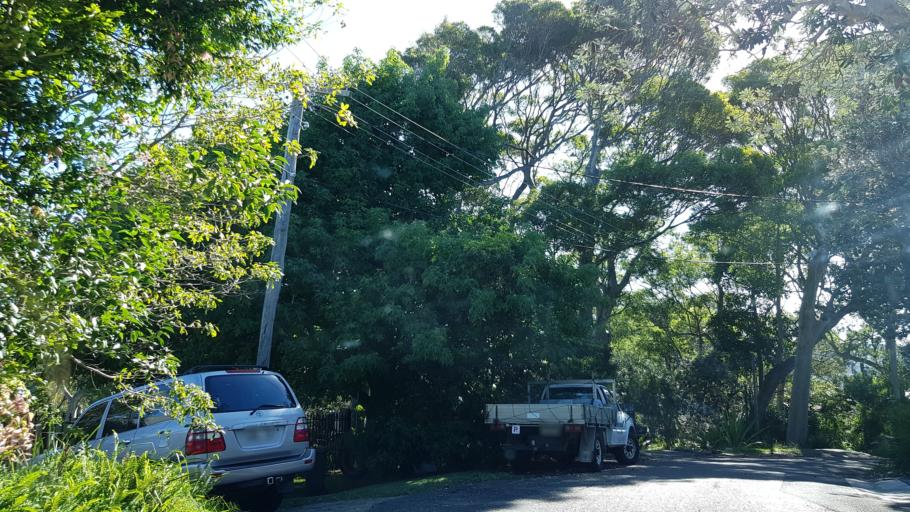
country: AU
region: New South Wales
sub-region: Pittwater
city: Palm Beach
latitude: -33.6163
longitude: 151.3310
